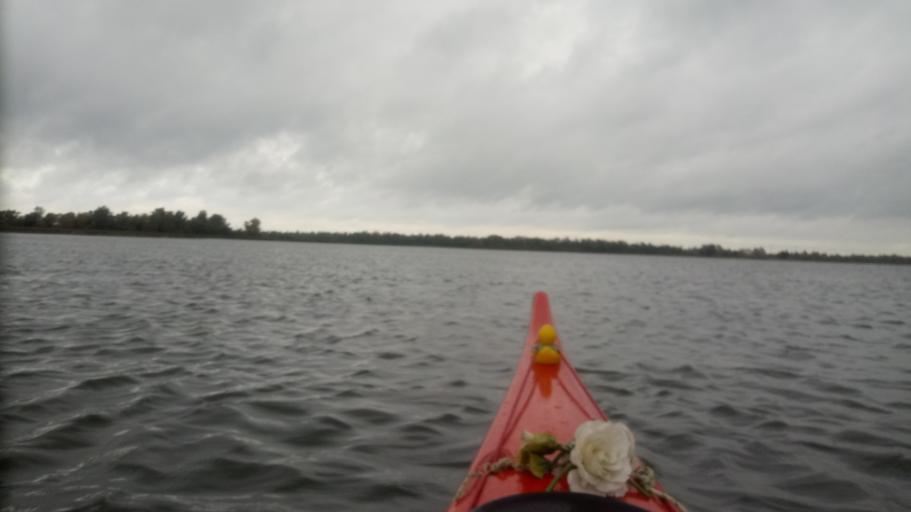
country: NL
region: North Brabant
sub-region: Gemeente Geertruidenberg
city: Geertruidenberg
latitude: 51.7365
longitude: 4.8409
